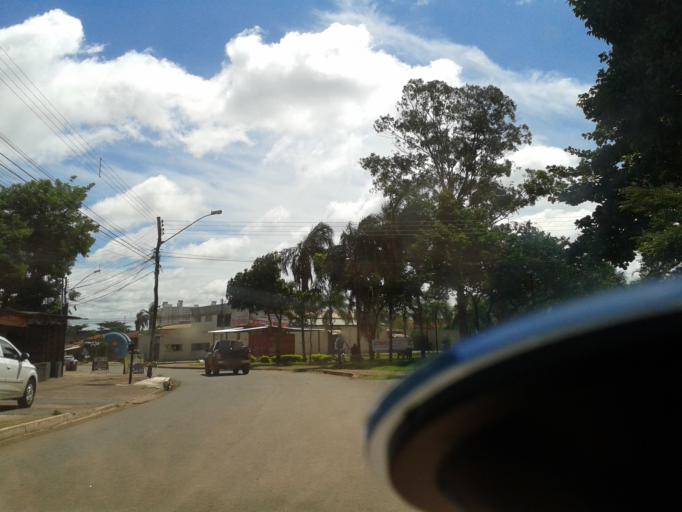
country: BR
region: Goias
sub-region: Goiania
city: Goiania
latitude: -16.6508
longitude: -49.3367
